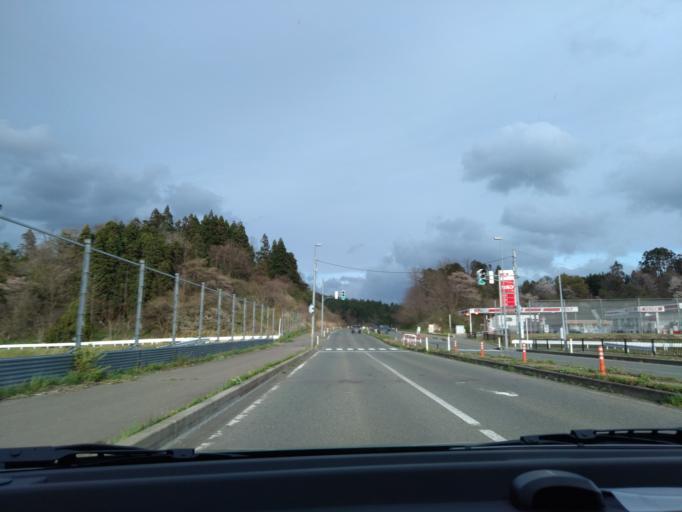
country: JP
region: Akita
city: Akita
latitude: 39.7521
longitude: 140.1170
